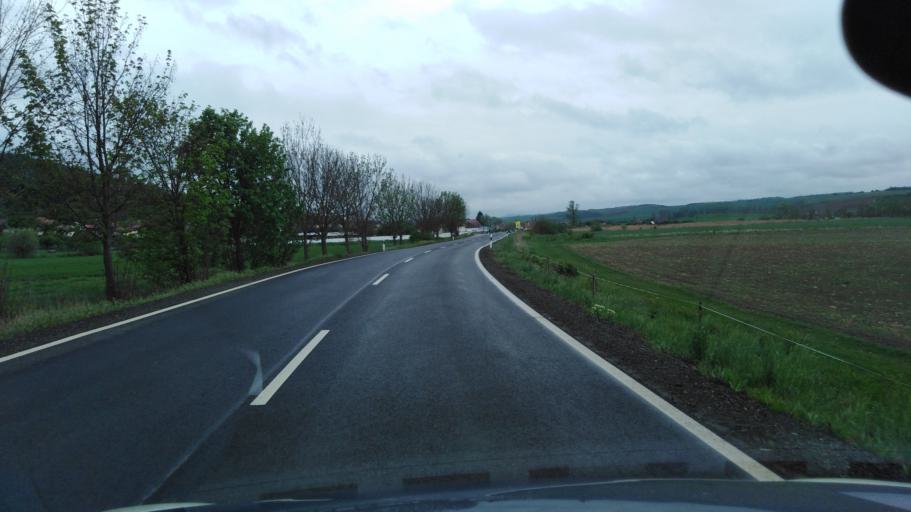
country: HU
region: Nograd
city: Karancskeszi
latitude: 48.1277
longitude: 19.6298
